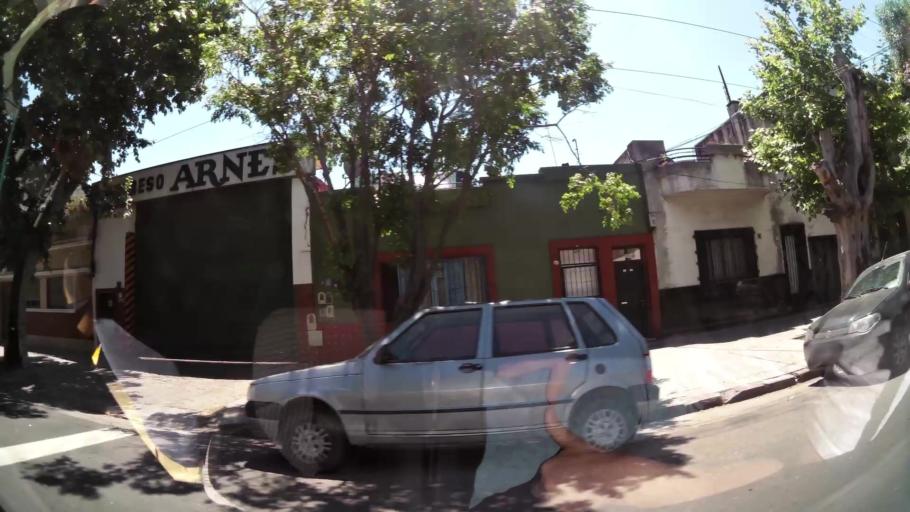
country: AR
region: Buenos Aires
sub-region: Partido de Avellaneda
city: Avellaneda
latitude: -34.6468
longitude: -58.3884
